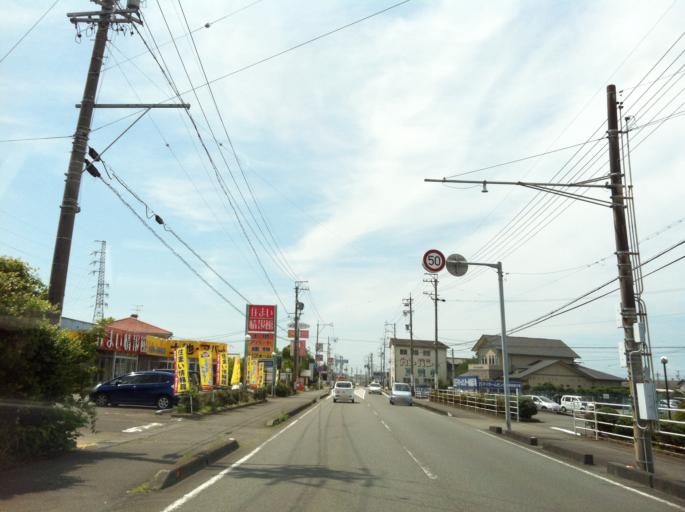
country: JP
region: Shizuoka
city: Shimada
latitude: 34.7865
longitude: 138.2540
